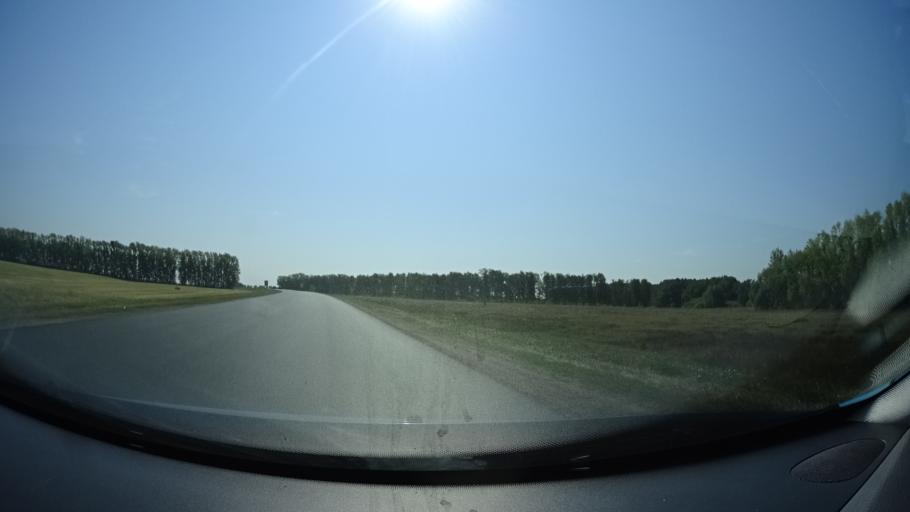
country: RU
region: Bashkortostan
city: Kabakovo
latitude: 54.4820
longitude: 55.9236
